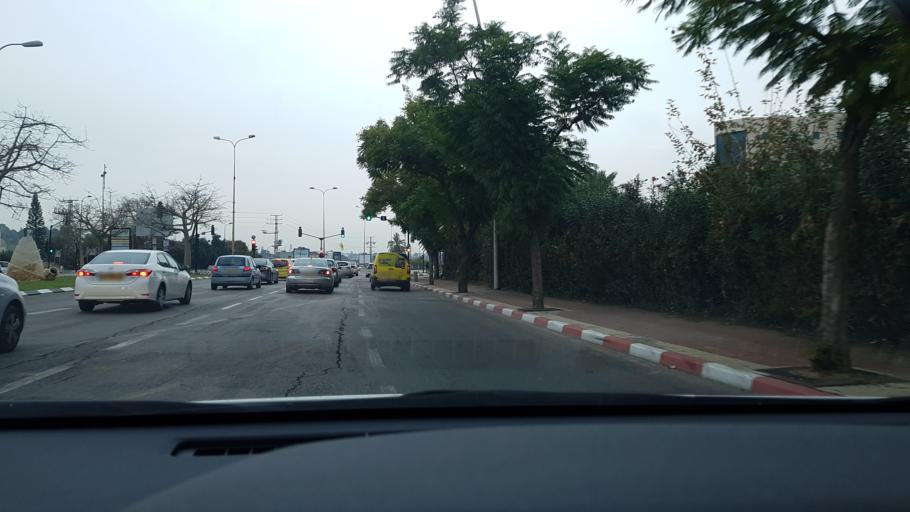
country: IL
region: Central District
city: Ness Ziona
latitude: 31.9109
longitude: 34.8037
